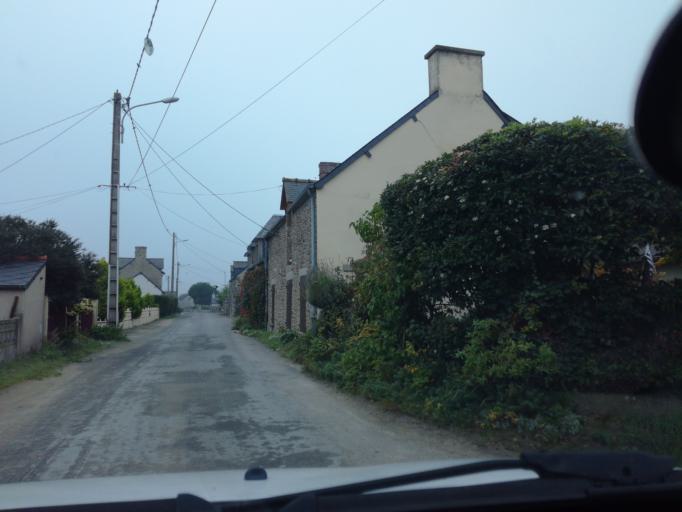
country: FR
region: Brittany
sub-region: Departement d'Ille-et-Vilaine
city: Cherrueix
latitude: 48.6062
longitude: -1.7117
